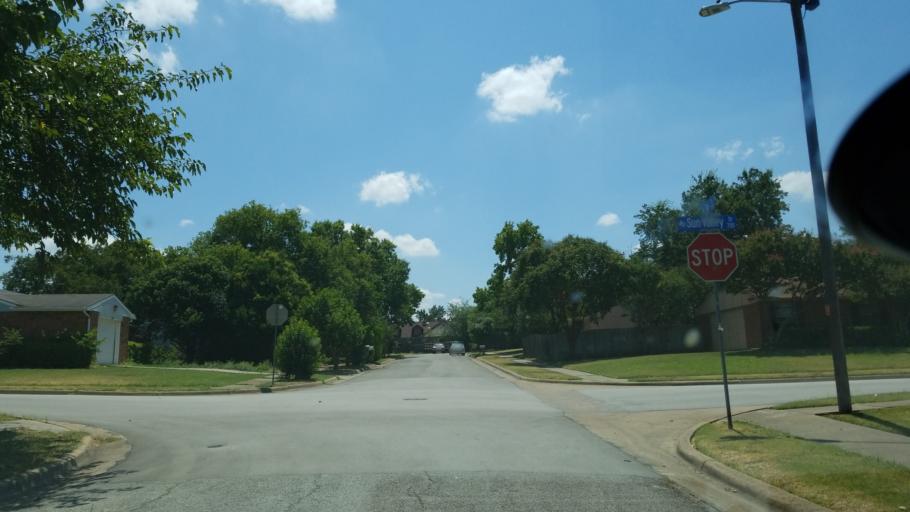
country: US
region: Texas
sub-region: Dallas County
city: Duncanville
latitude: 32.6683
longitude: -96.8921
